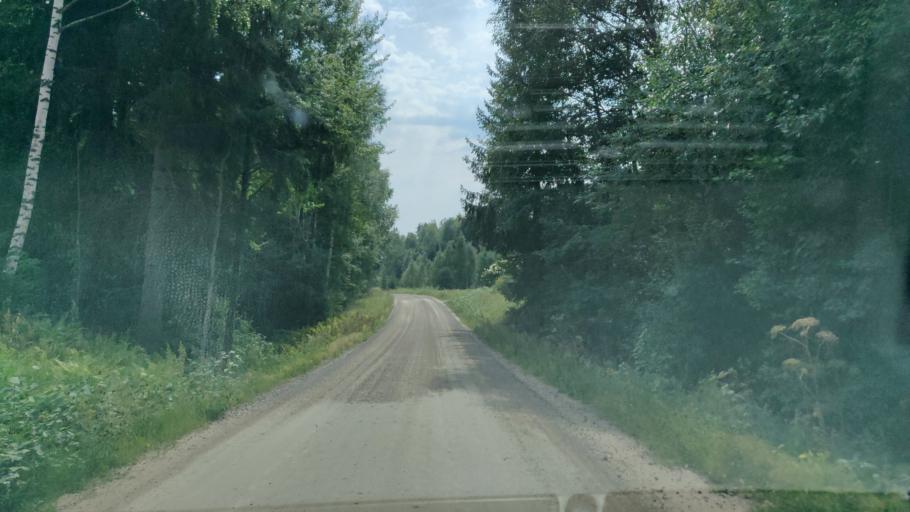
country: SE
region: Vaermland
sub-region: Munkfors Kommun
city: Munkfors
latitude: 59.9192
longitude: 13.5489
